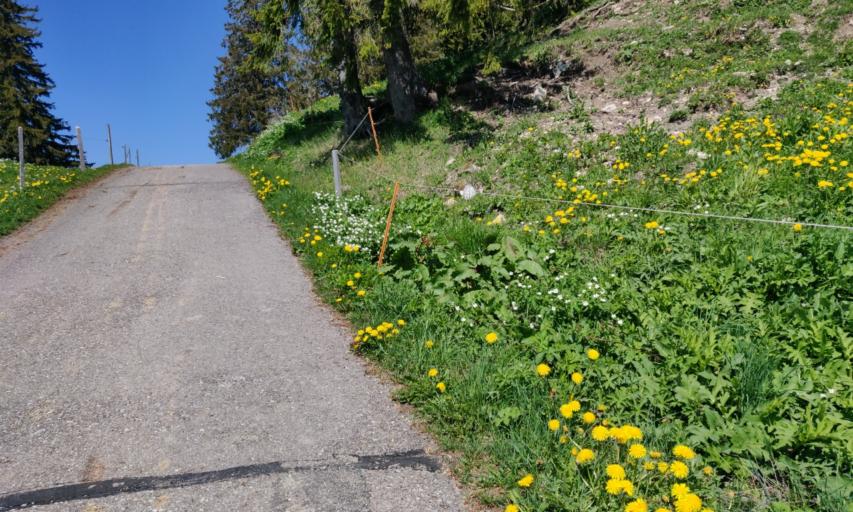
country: CH
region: Fribourg
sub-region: Gruyere District
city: Vuadens
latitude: 46.5398
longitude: 6.9907
